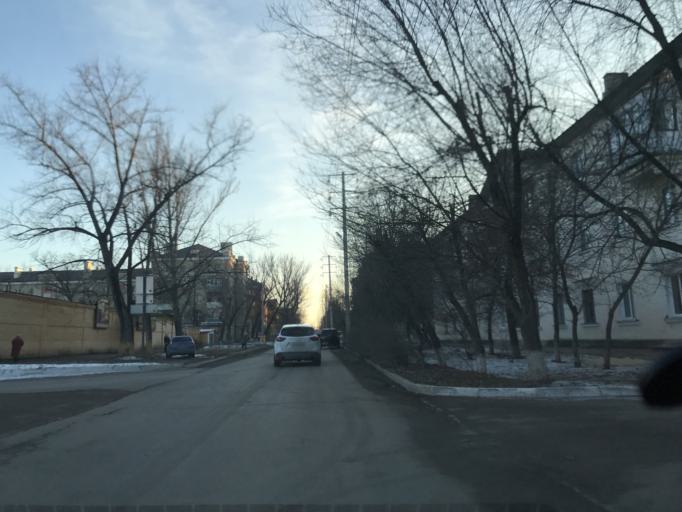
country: RU
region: Rostov
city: Kamensk-Shakhtinskiy
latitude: 48.3195
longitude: 40.2642
